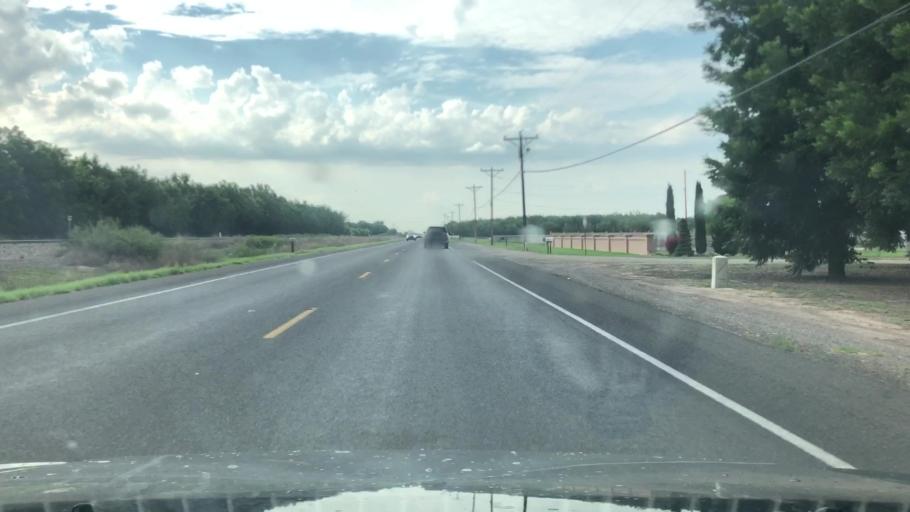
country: US
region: New Mexico
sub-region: Dona Ana County
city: San Miguel
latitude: 32.2173
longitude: -106.7298
